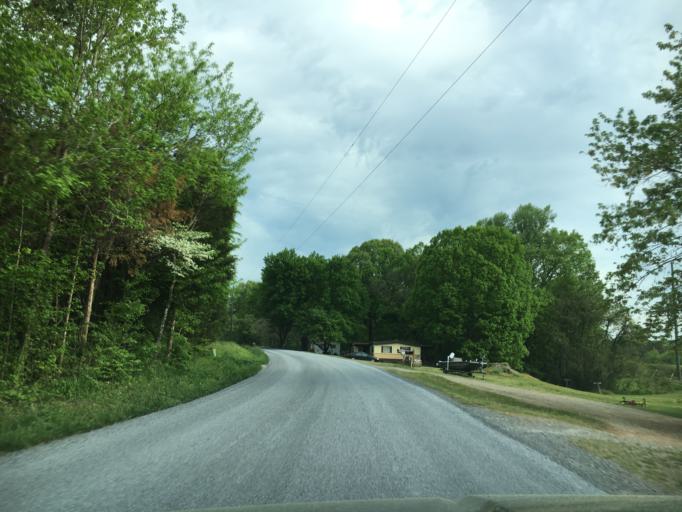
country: US
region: Virginia
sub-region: Campbell County
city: Brookneal
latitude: 36.9518
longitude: -78.9681
